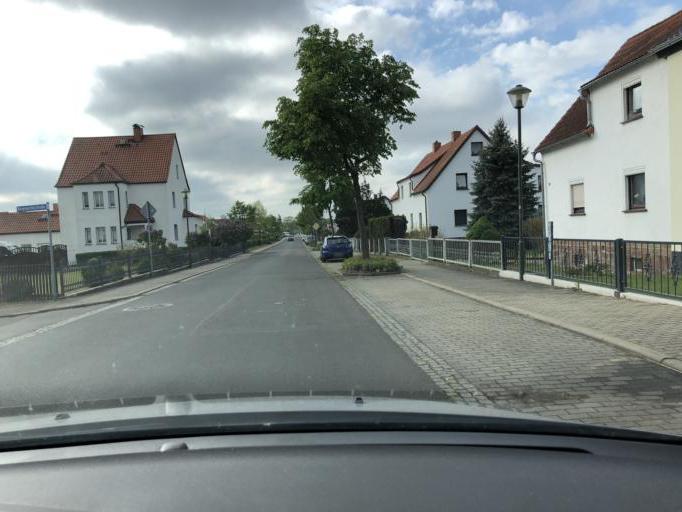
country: DE
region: Saxony
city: Lobstadt
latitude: 51.1308
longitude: 12.4516
